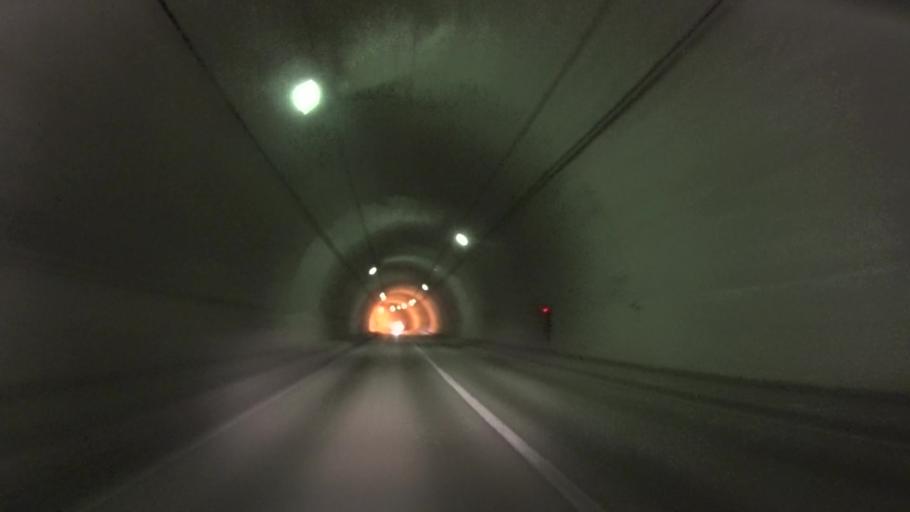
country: JP
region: Kyoto
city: Miyazu
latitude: 35.7305
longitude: 135.0921
